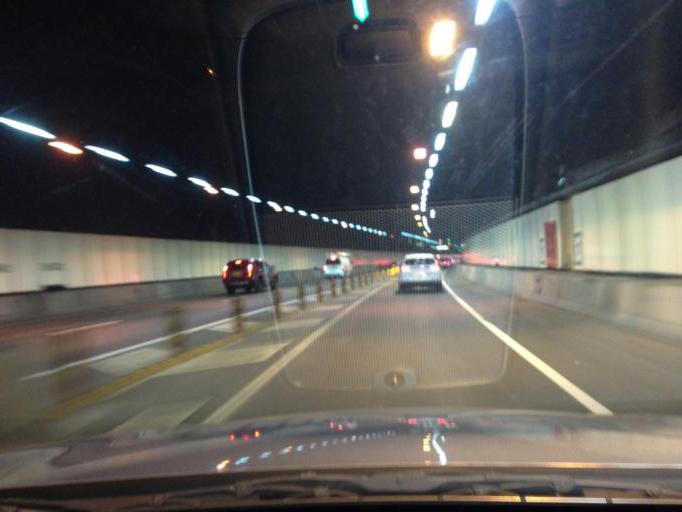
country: AU
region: New South Wales
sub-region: City of Sydney
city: Darlinghurst
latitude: -33.8841
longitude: 151.2177
